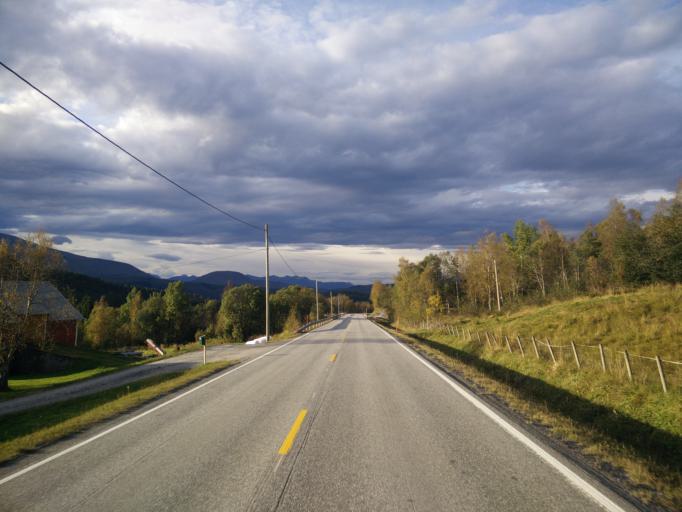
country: NO
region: More og Romsdal
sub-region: Molde
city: Hjelset
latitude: 62.8075
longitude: 7.5819
